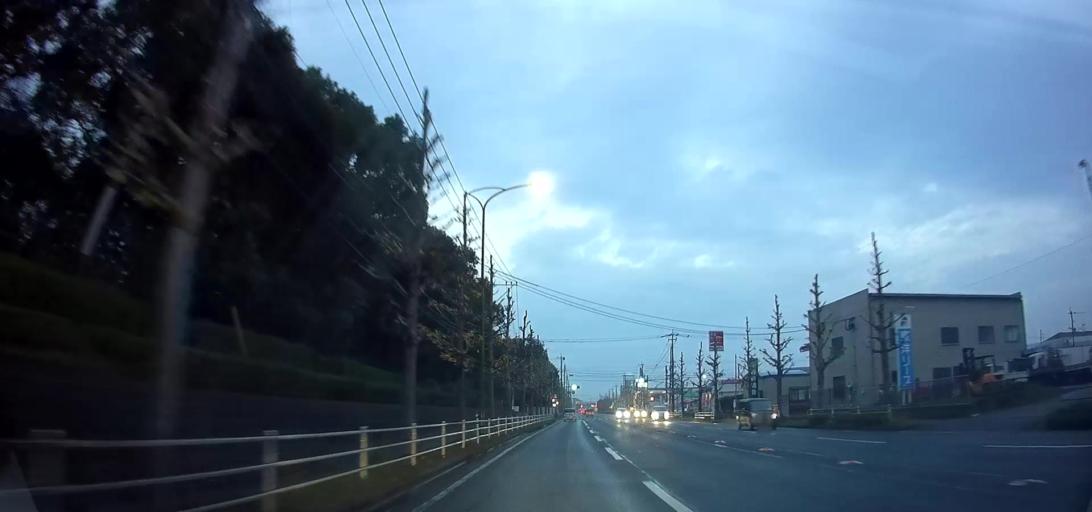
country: JP
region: Nagasaki
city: Omura
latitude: 32.9176
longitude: 129.9423
